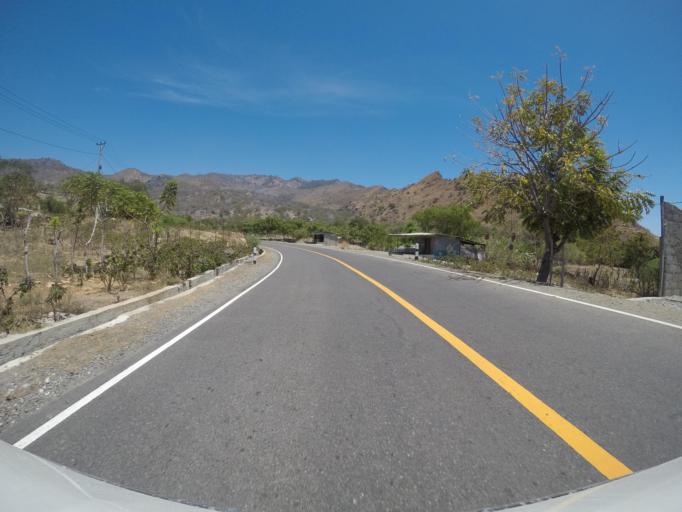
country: TL
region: Manatuto
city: Manatuto
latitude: -8.4889
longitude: 125.9702
